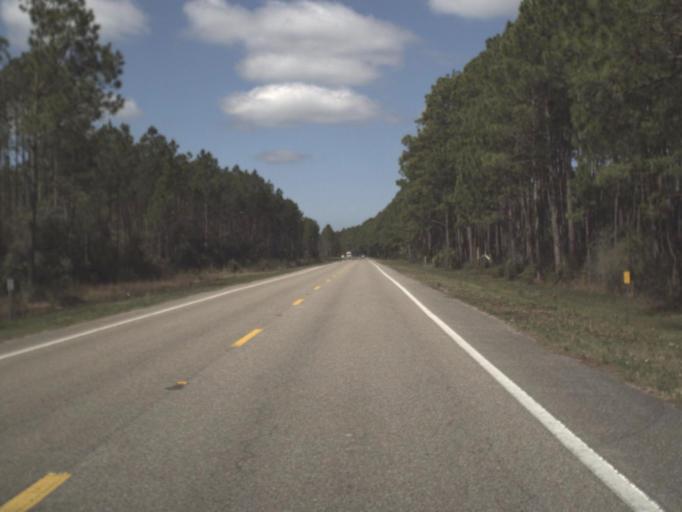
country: US
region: Florida
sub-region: Franklin County
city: Apalachicola
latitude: 29.7332
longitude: -85.1476
